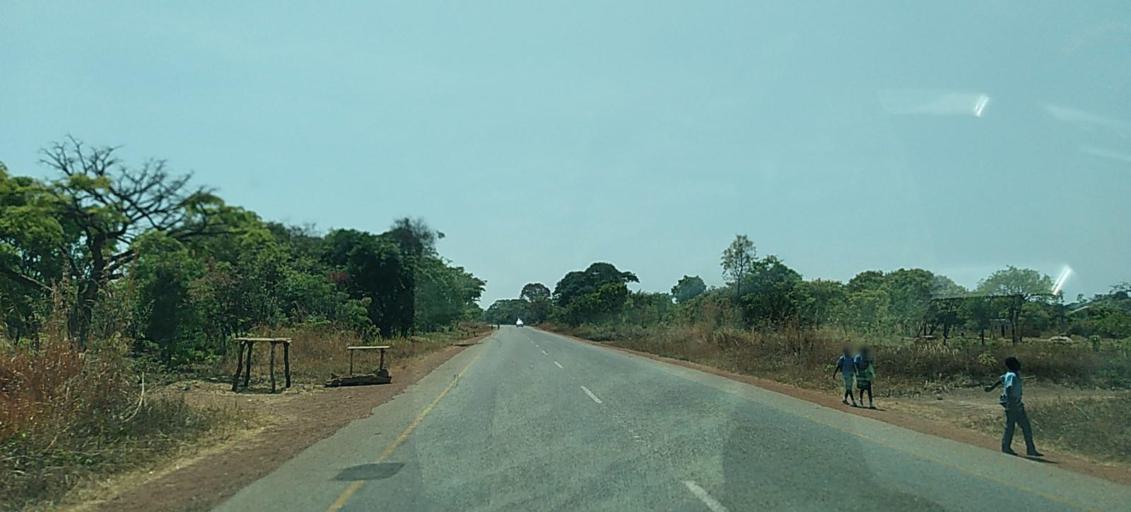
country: ZM
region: North-Western
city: Solwezi
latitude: -12.4092
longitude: 26.1251
